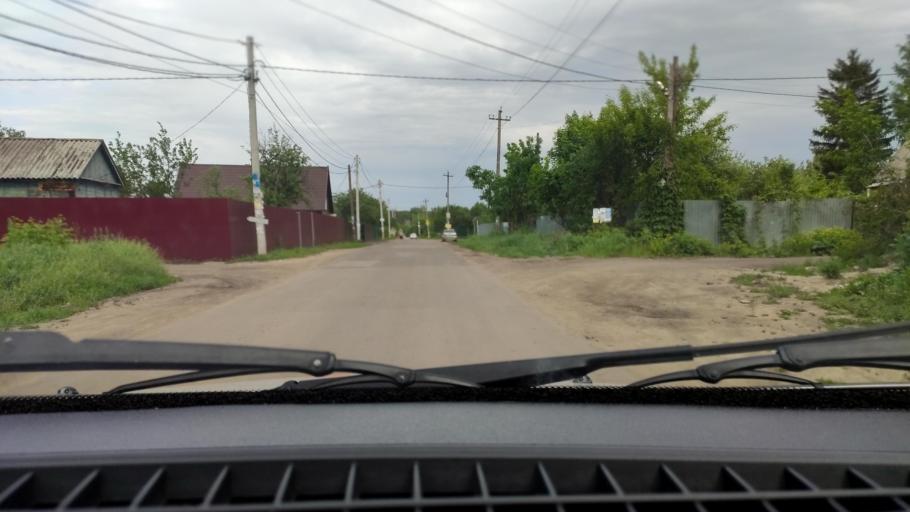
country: RU
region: Voronezj
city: Shilovo
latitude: 51.5997
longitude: 39.1446
